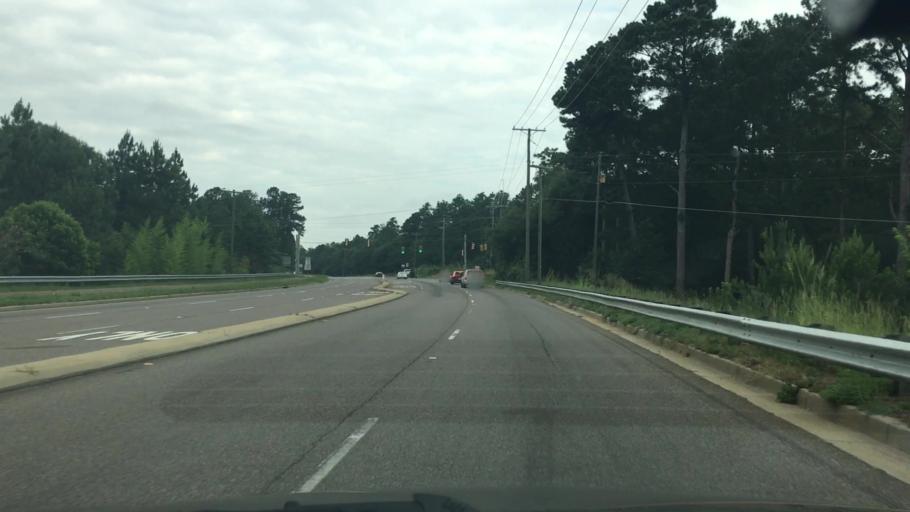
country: US
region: South Carolina
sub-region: Aiken County
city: Aiken
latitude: 33.5714
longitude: -81.6921
